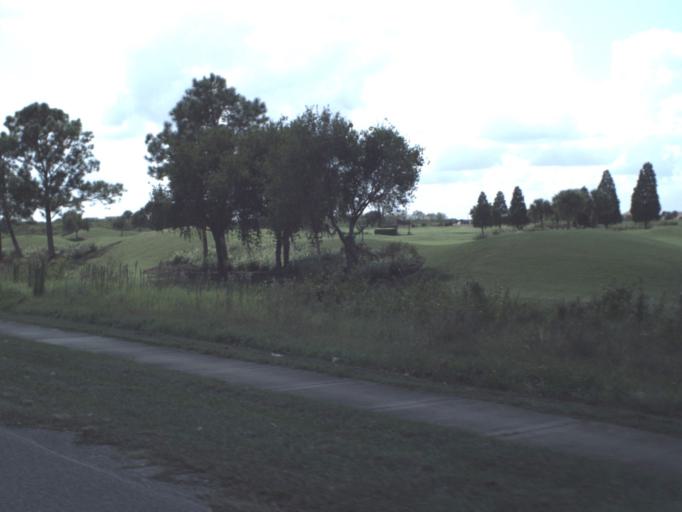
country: US
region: Florida
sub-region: Polk County
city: Lakeland
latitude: 28.0106
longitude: -81.9752
